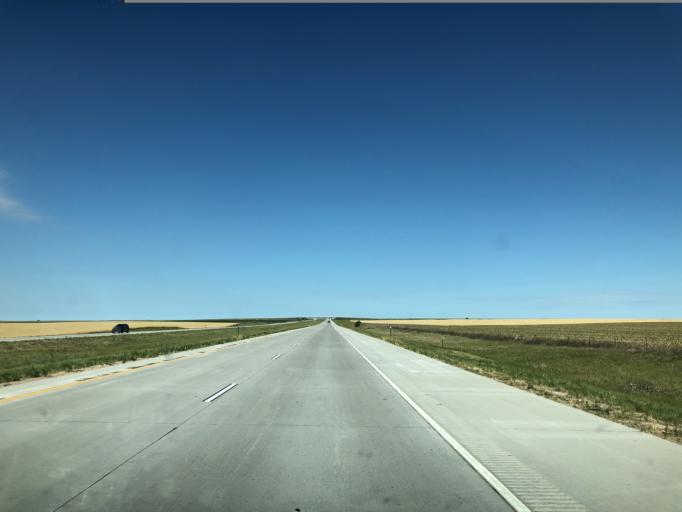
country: US
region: Colorado
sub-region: Kit Carson County
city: Burlington
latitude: 39.2942
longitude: -102.7641
